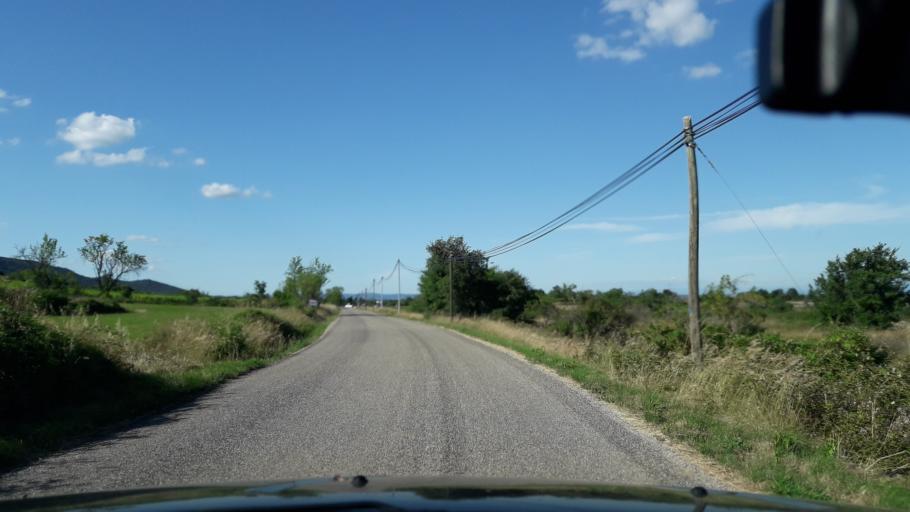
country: FR
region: Languedoc-Roussillon
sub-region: Departement du Gard
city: Saint-Julien-de-Peyrolas
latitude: 44.3860
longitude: 4.5103
